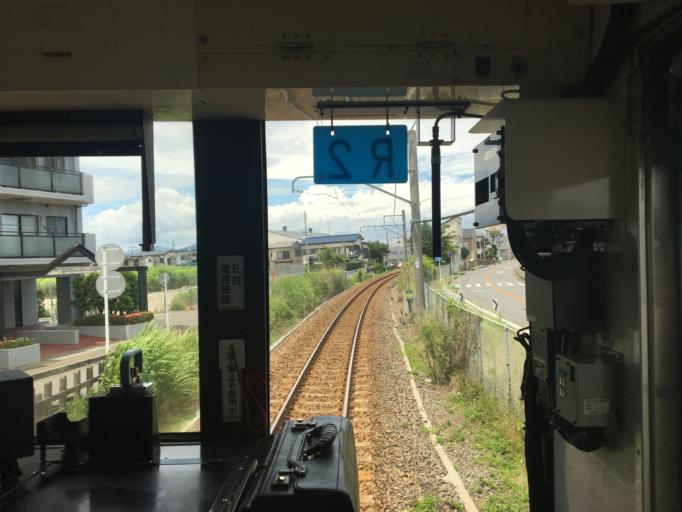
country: JP
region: Kanagawa
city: Atsugi
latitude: 35.4098
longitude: 139.3784
